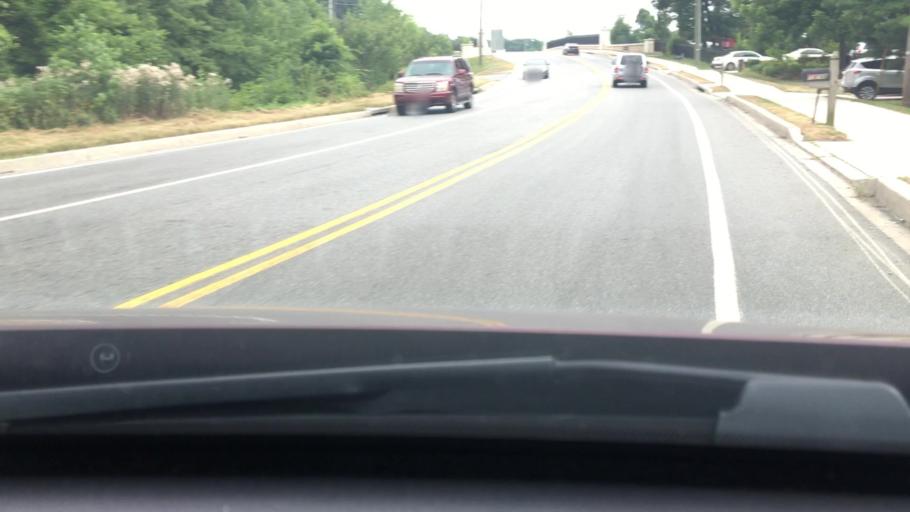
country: US
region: Maryland
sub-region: Prince George's County
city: Calverton
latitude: 39.0754
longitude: -76.9211
